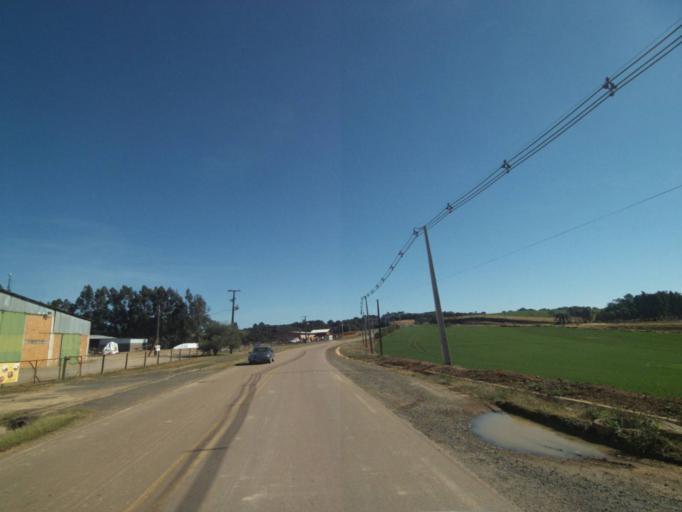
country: BR
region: Parana
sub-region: Tibagi
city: Tibagi
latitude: -24.5265
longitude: -50.4410
